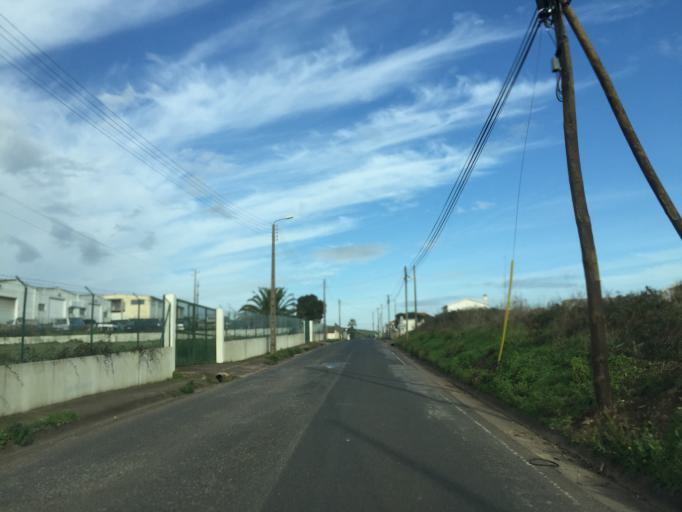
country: PT
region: Lisbon
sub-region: Sintra
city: Almargem
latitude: 38.8448
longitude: -9.2608
